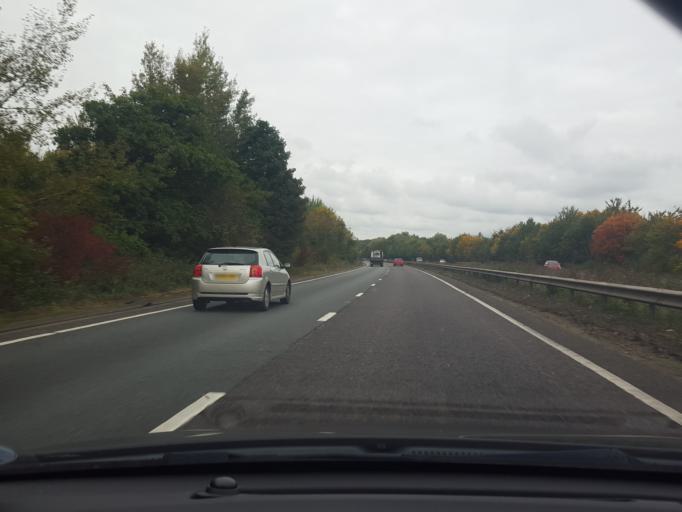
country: GB
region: England
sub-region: Suffolk
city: Bramford
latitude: 52.1243
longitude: 1.0991
